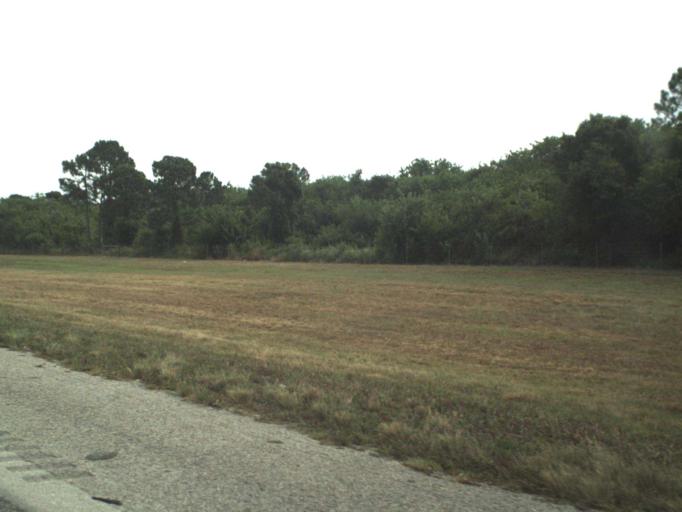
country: US
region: Florida
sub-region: Saint Lucie County
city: Port Saint Lucie
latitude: 27.2016
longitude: -80.4003
